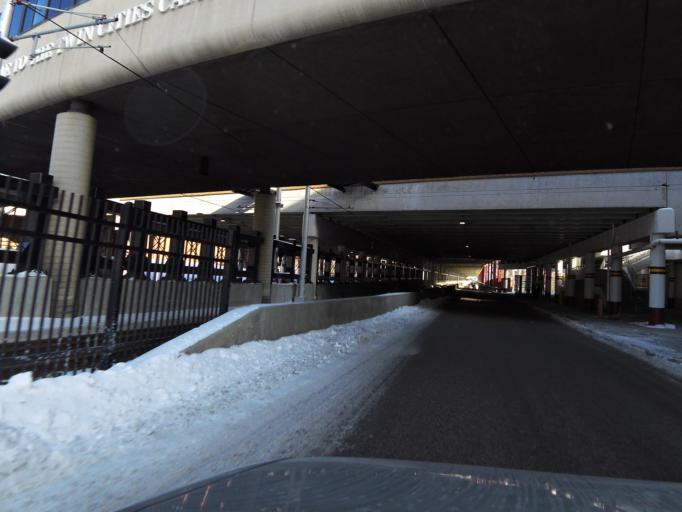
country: US
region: Minnesota
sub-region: Hennepin County
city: Minneapolis
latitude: 44.9724
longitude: -93.2435
